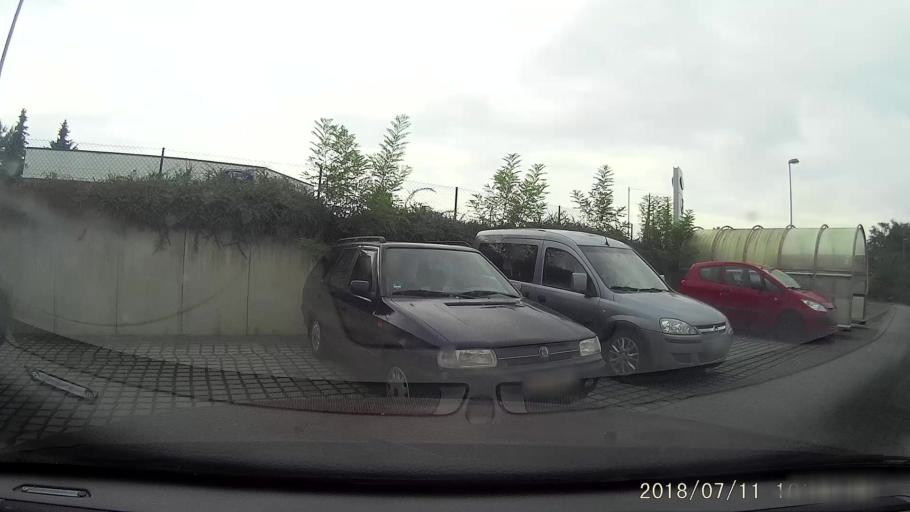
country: DE
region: Saxony
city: Niesky
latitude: 51.2875
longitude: 14.8184
